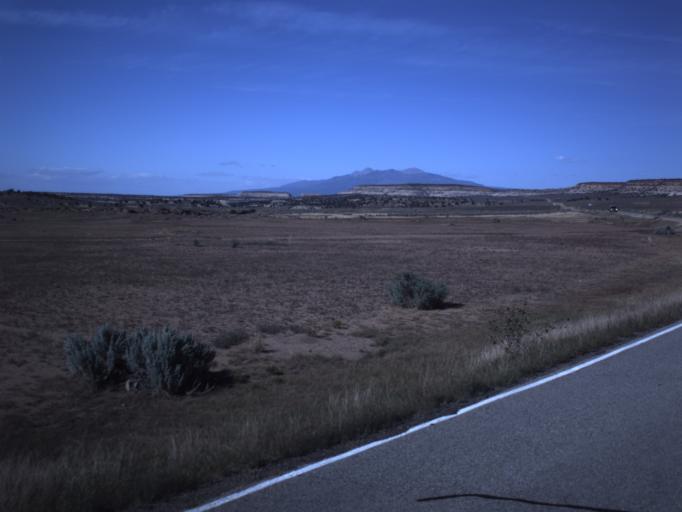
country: US
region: Utah
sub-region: San Juan County
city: Monticello
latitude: 38.0090
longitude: -109.4365
